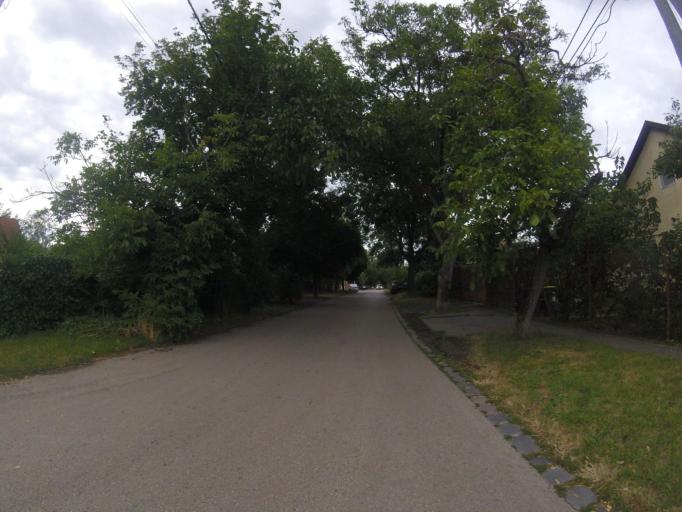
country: HU
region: Pest
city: Budakalasz
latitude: 47.5886
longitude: 19.0594
